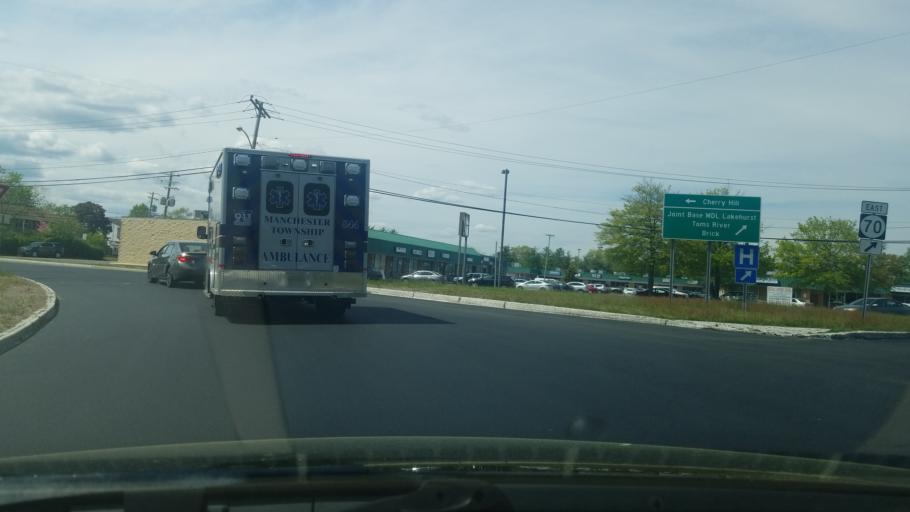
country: US
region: New Jersey
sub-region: Ocean County
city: Lakehurst
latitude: 40.0120
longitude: -74.3252
